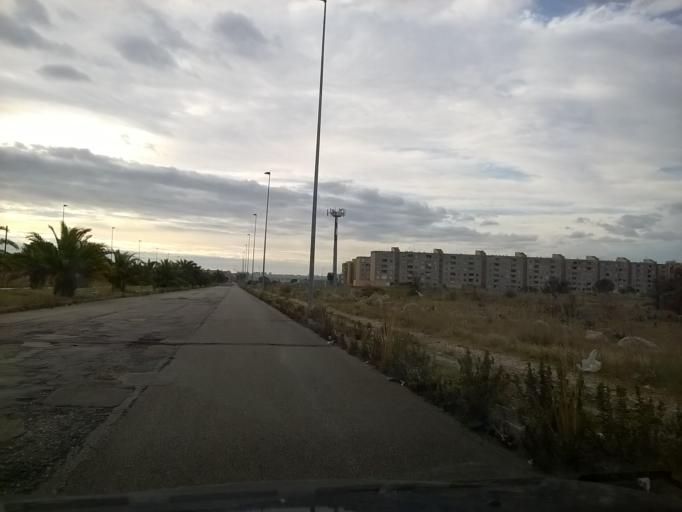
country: IT
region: Apulia
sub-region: Provincia di Taranto
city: Paolo VI
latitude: 40.5322
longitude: 17.2767
